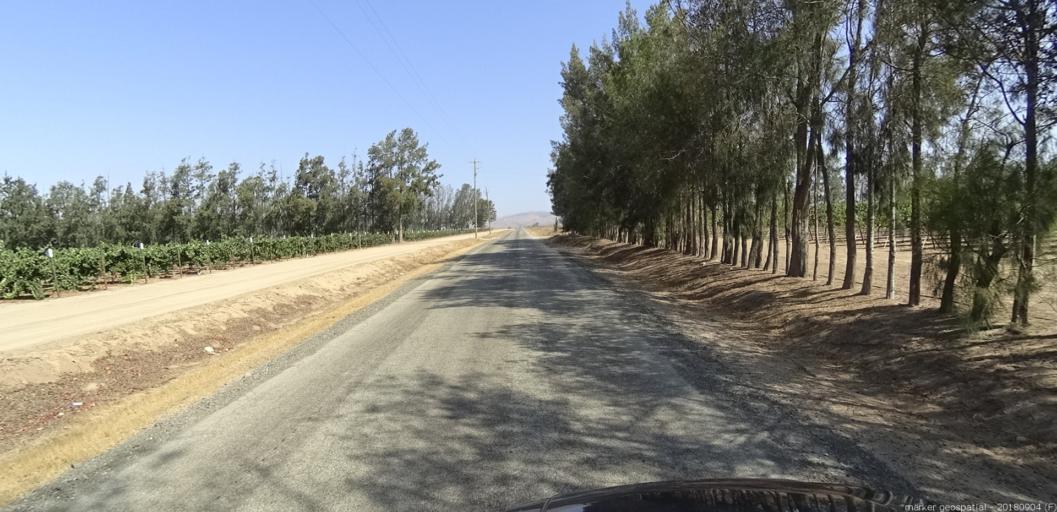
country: US
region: California
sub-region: Monterey County
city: Gonzales
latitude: 36.4955
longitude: -121.3648
